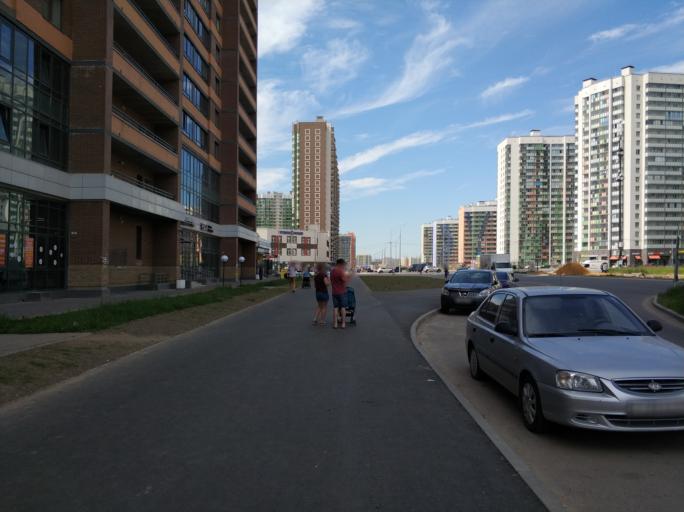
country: RU
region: Leningrad
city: Murino
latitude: 60.0571
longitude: 30.4314
